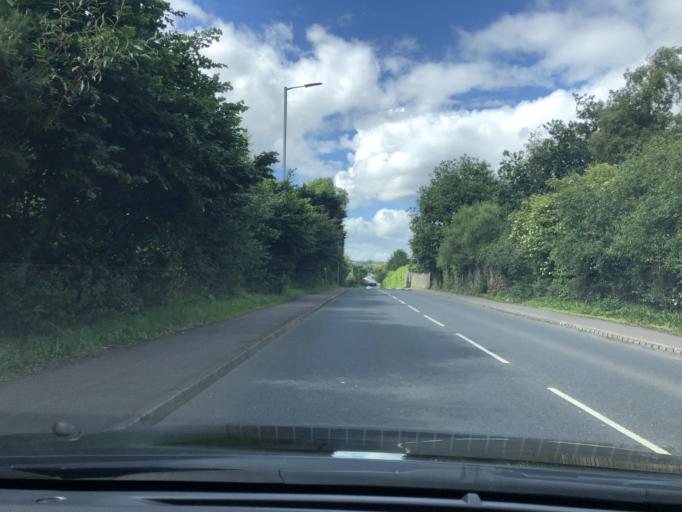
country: GB
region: Northern Ireland
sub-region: Ards District
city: Newtownards
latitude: 54.5853
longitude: -5.7117
